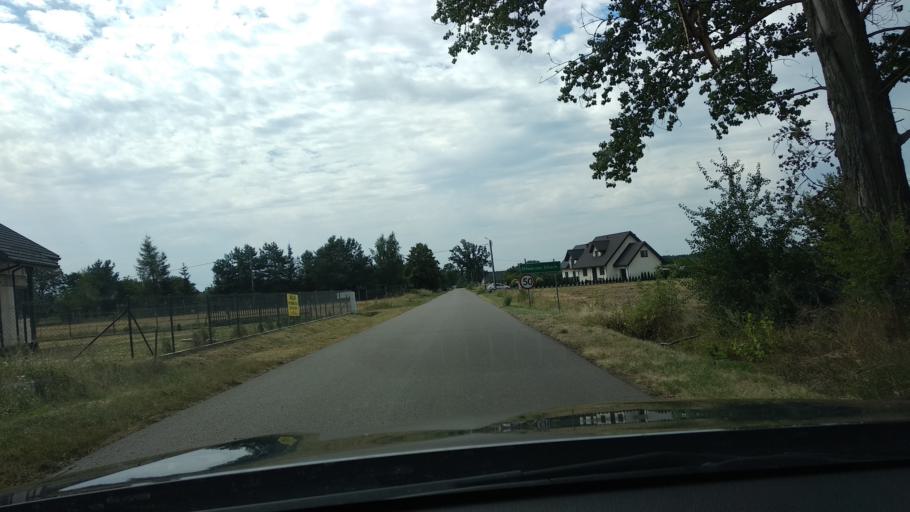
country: PL
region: Masovian Voivodeship
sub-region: Powiat pultuski
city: Zatory
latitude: 52.6540
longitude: 21.1867
